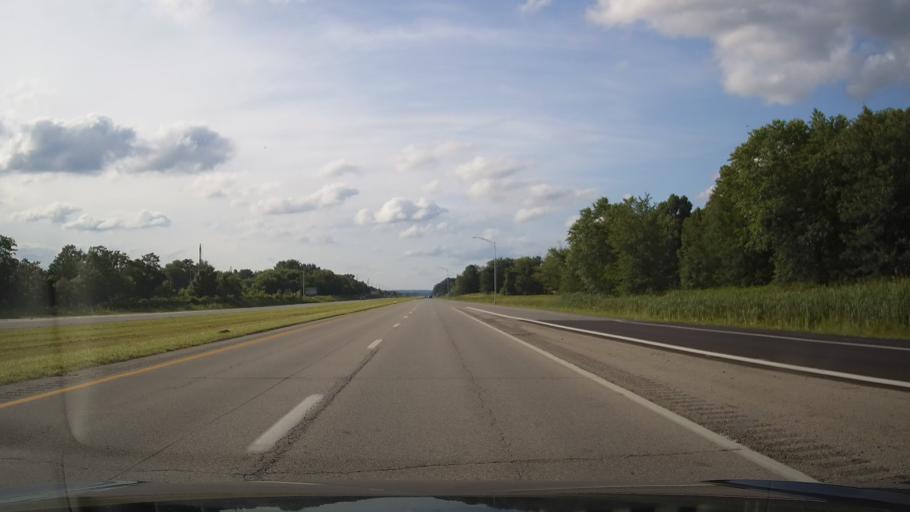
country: US
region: Ohio
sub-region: Scioto County
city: Franklin Furnace
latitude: 38.6511
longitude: -82.8514
